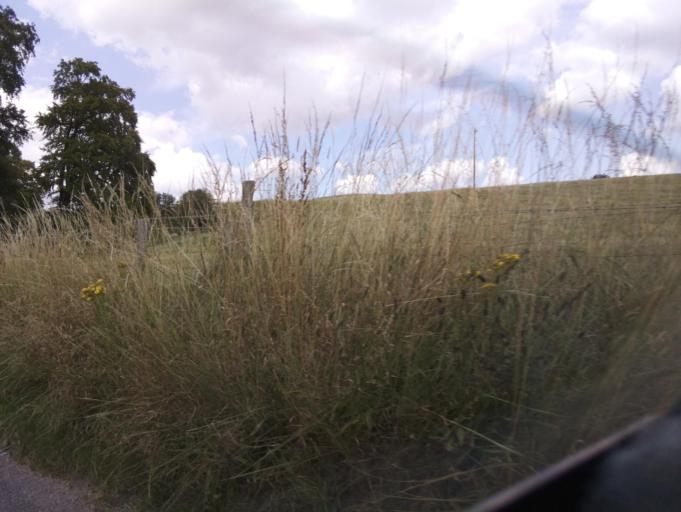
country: GB
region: England
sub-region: Wiltshire
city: Aldbourne
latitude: 51.5281
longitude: -1.5851
